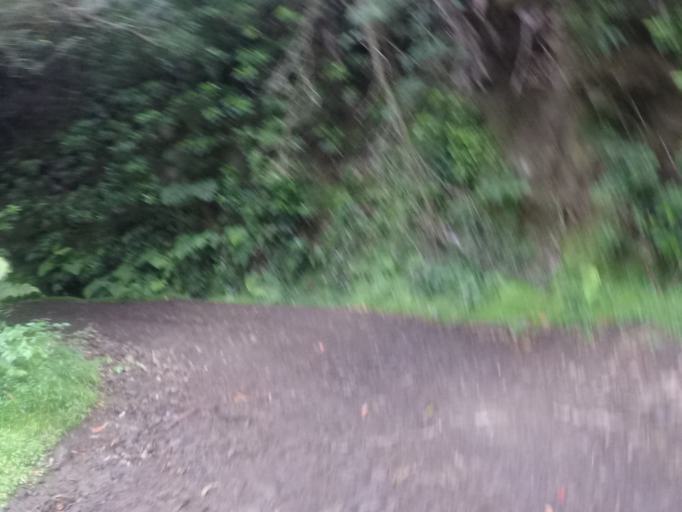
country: PT
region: Madeira
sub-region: Santana
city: Santana
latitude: 32.7762
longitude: -16.8789
